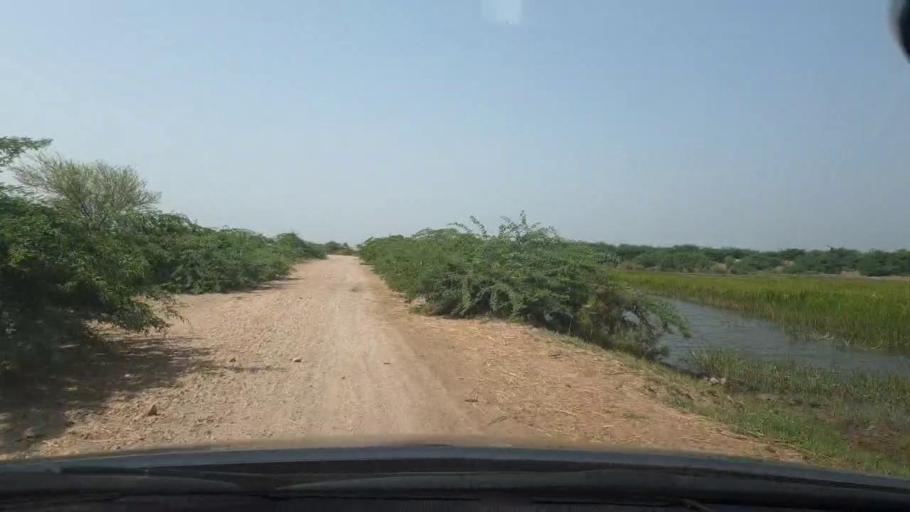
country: PK
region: Sindh
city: Tando Bago
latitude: 24.7181
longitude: 69.0934
